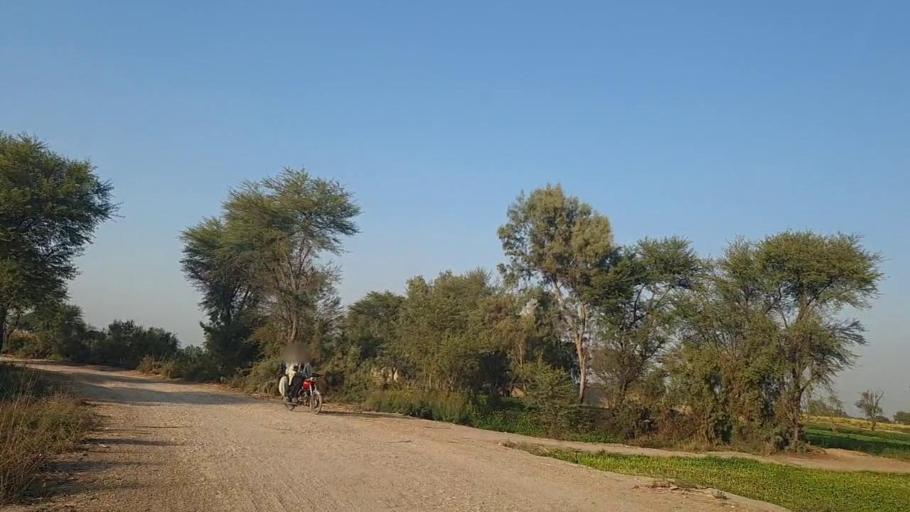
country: PK
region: Sindh
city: Sakrand
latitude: 26.3035
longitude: 68.1266
